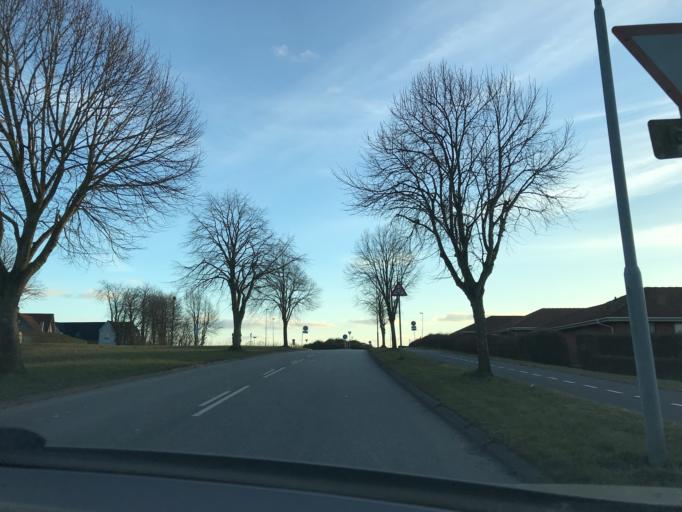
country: DK
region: South Denmark
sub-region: Middelfart Kommune
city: Norre Aby
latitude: 55.4545
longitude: 9.8794
